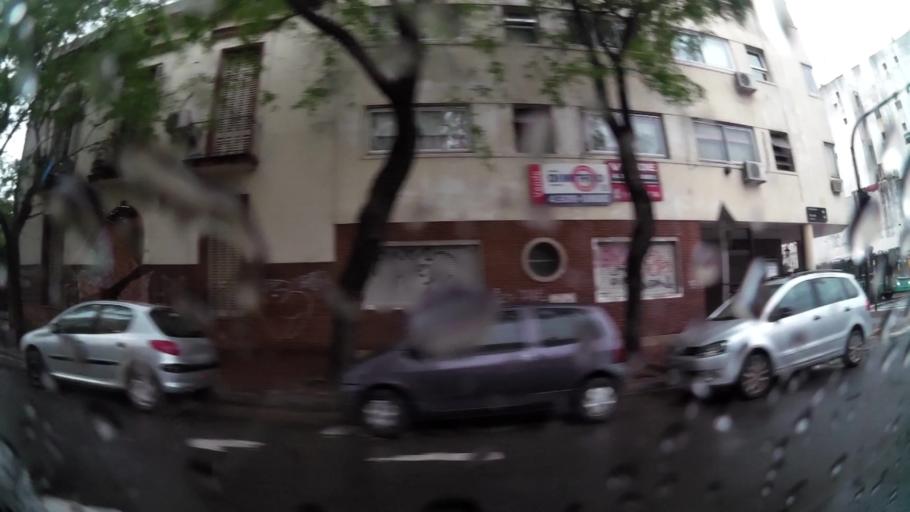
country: AR
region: Buenos Aires F.D.
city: Buenos Aires
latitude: -34.6272
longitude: -58.3754
